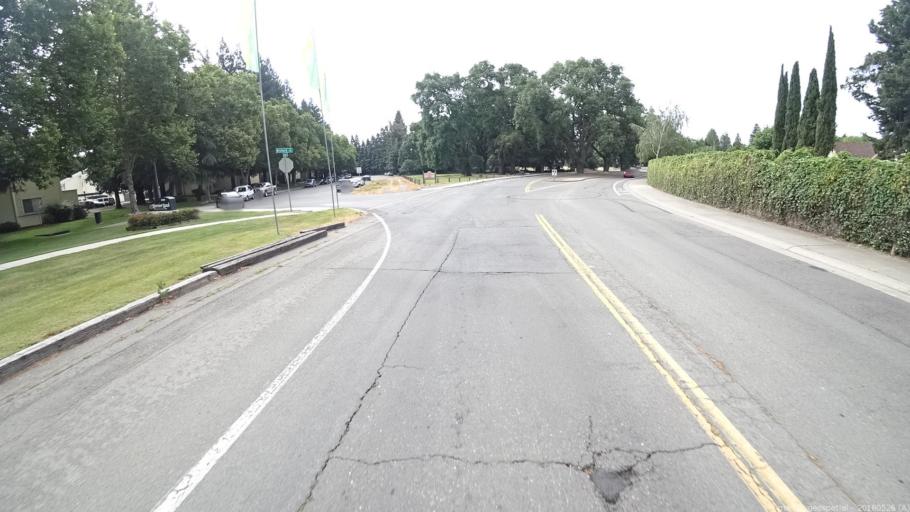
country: US
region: California
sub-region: Yolo County
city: West Sacramento
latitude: 38.6091
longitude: -121.5292
